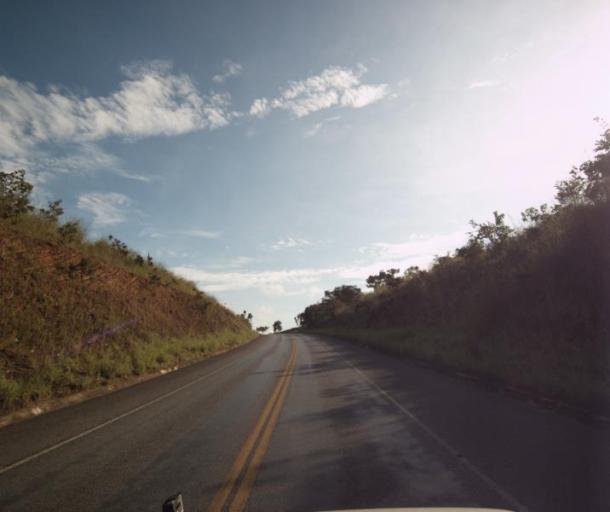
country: BR
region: Goias
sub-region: Pirenopolis
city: Pirenopolis
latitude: -15.5703
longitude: -48.6221
